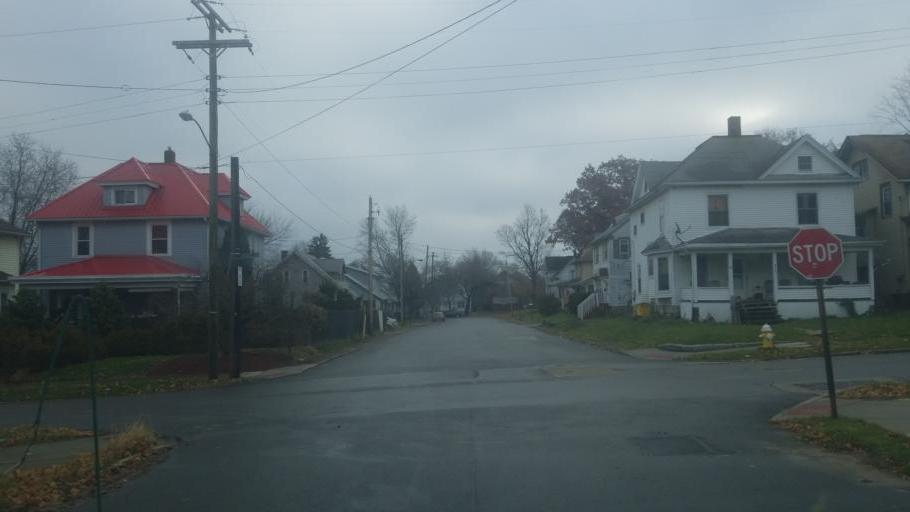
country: US
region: Ohio
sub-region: Richland County
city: Mansfield
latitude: 40.7619
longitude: -82.5352
